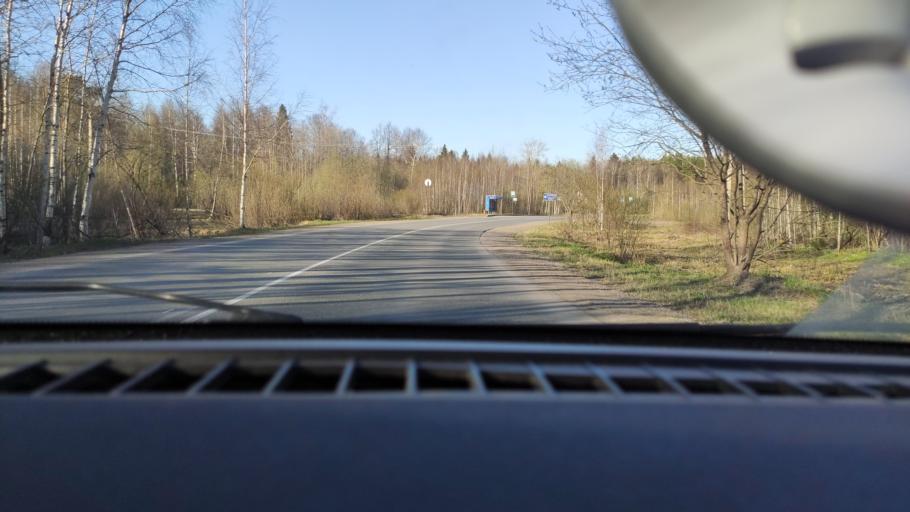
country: RU
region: Perm
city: Polazna
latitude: 58.1229
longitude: 56.4336
